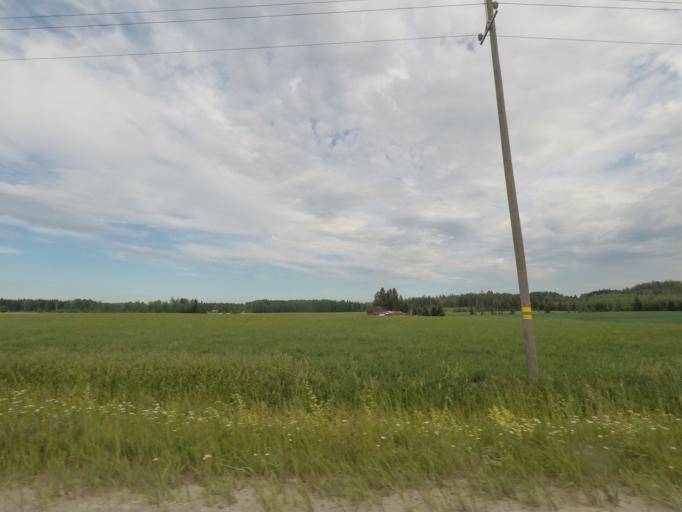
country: FI
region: Paijanne Tavastia
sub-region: Lahti
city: Lahti
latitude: 60.9246
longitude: 25.5778
